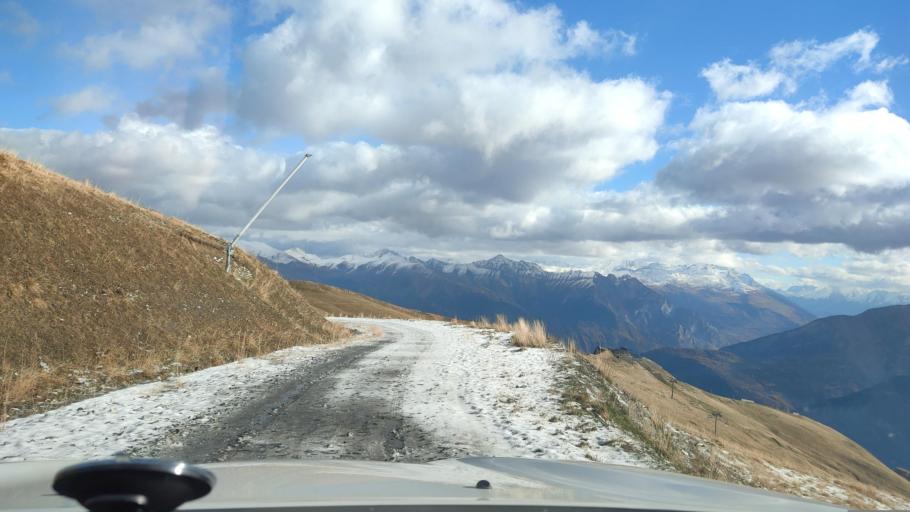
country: FR
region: Rhone-Alpes
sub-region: Departement de la Savoie
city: Saint-Etienne-de-Cuines
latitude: 45.2533
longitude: 6.2289
